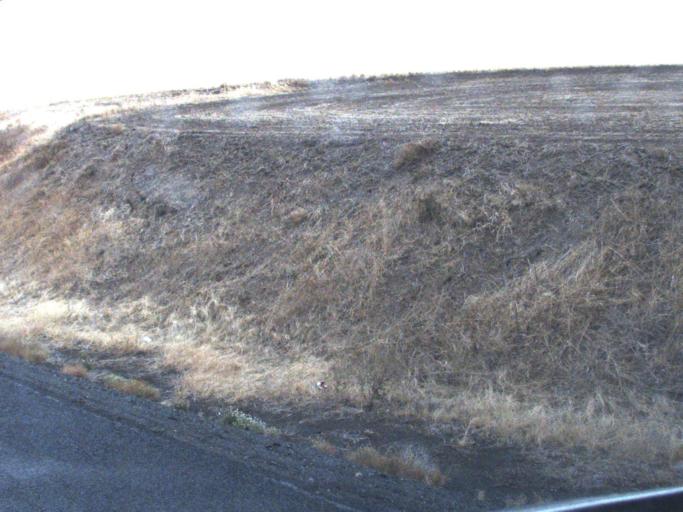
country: US
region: Washington
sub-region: Whitman County
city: Pullman
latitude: 46.6375
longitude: -117.1773
